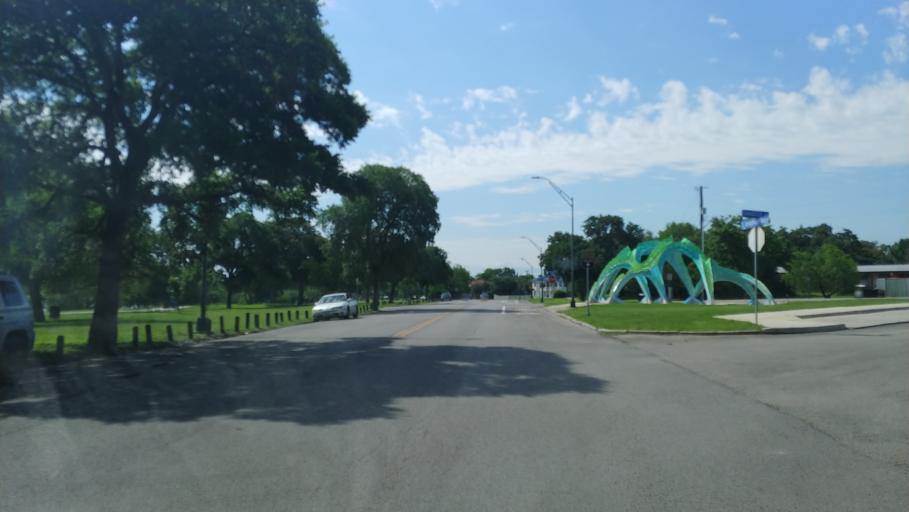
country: US
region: Texas
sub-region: Bexar County
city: Balcones Heights
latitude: 29.4513
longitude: -98.5353
